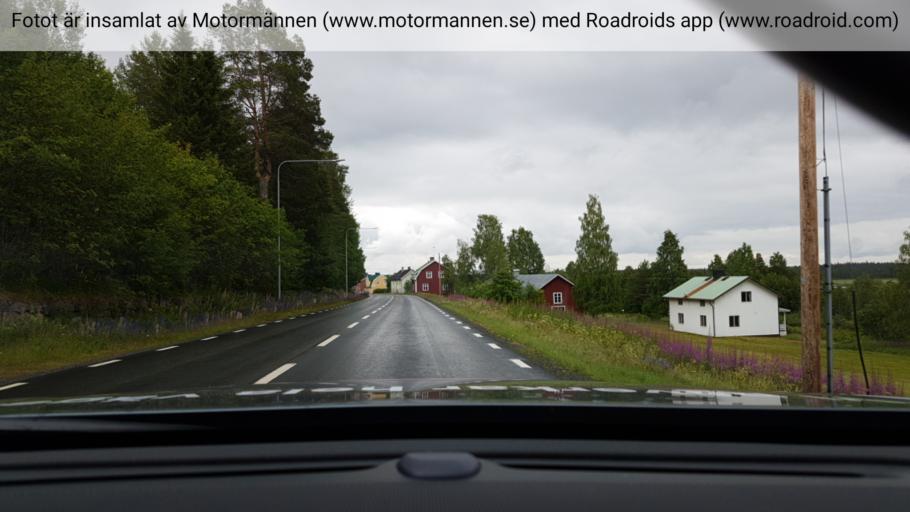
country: SE
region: Vaesterbotten
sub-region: Norsjo Kommun
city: Norsjoe
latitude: 65.2641
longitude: 19.6162
